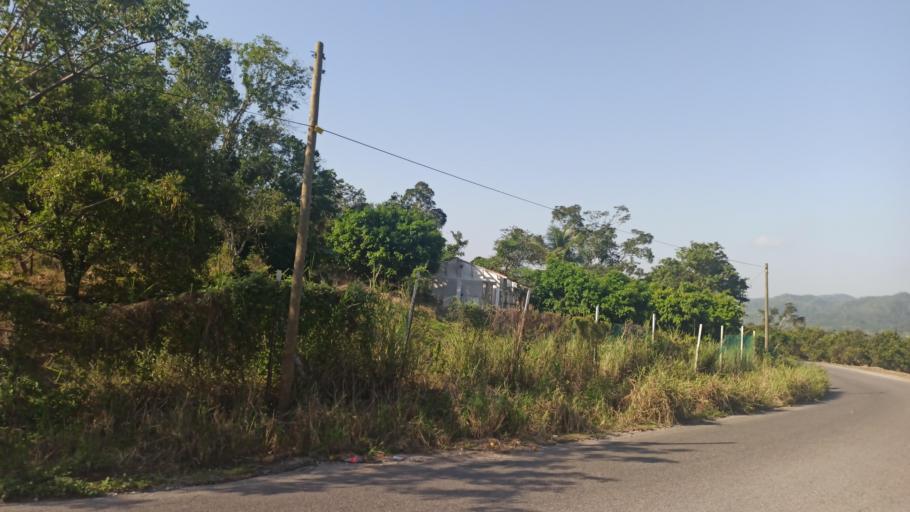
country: MX
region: Veracruz
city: Agua Dulce
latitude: 20.3946
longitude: -97.2398
